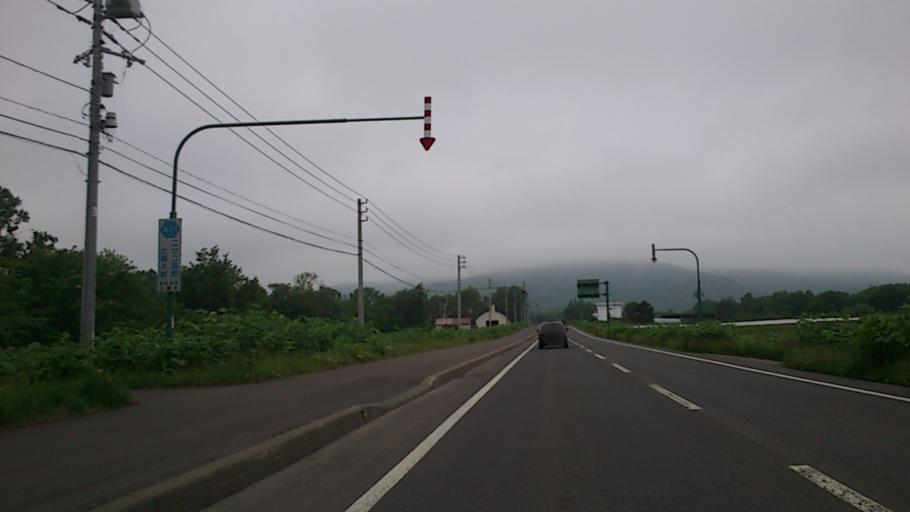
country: JP
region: Hokkaido
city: Niseko Town
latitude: 42.8636
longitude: 140.7438
